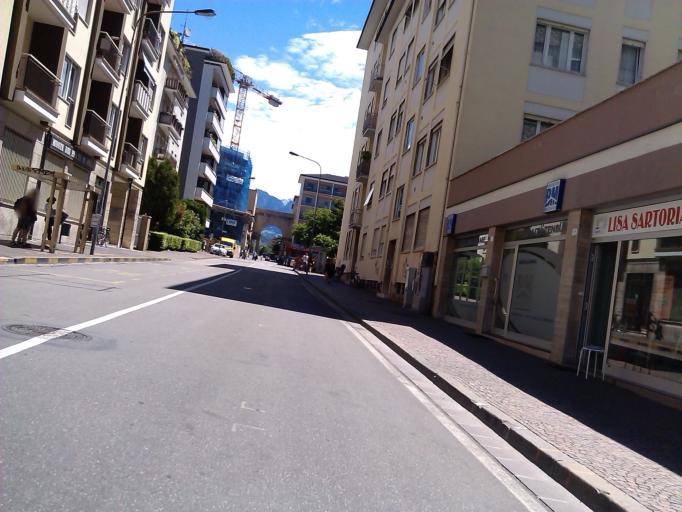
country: IT
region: Trentino-Alto Adige
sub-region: Bolzano
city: Bolzano
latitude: 46.5005
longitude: 11.3401
